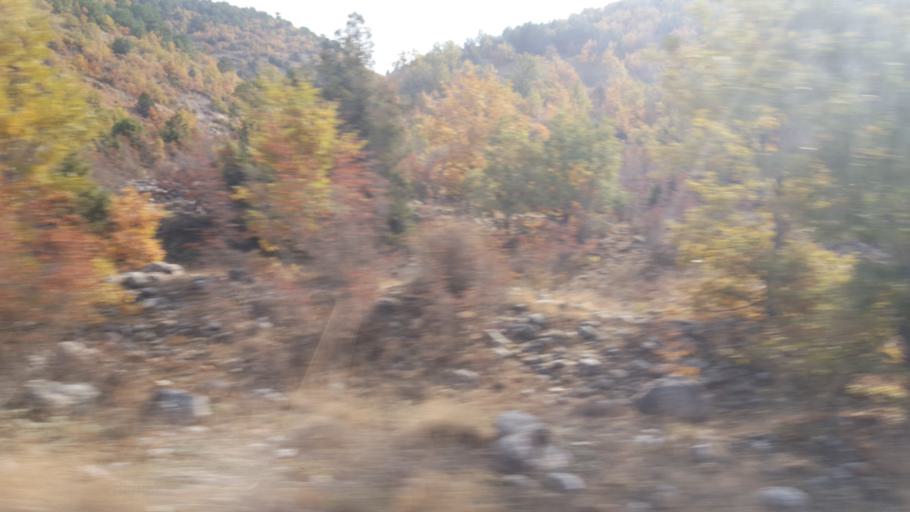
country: TR
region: Eskisehir
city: Mihaliccik
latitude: 39.9758
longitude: 31.3803
